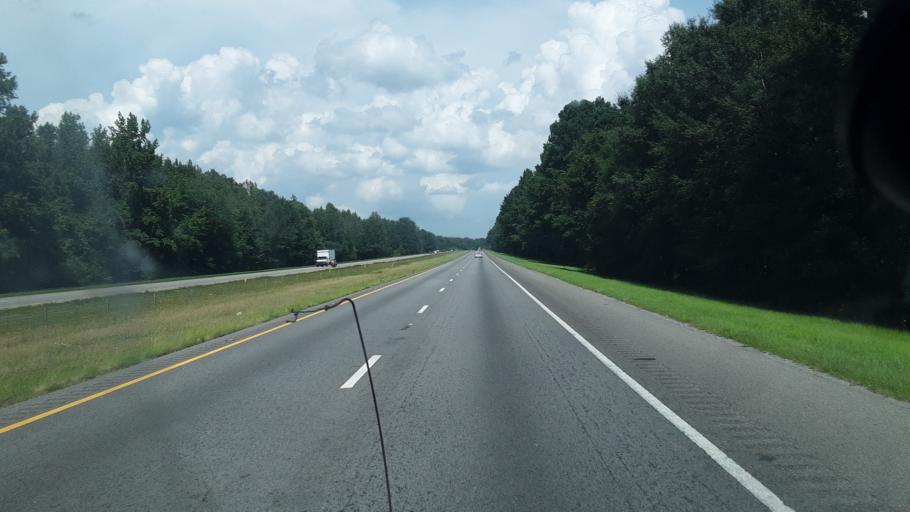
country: US
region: South Carolina
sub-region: Kershaw County
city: Lugoff
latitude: 34.2070
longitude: -80.6510
